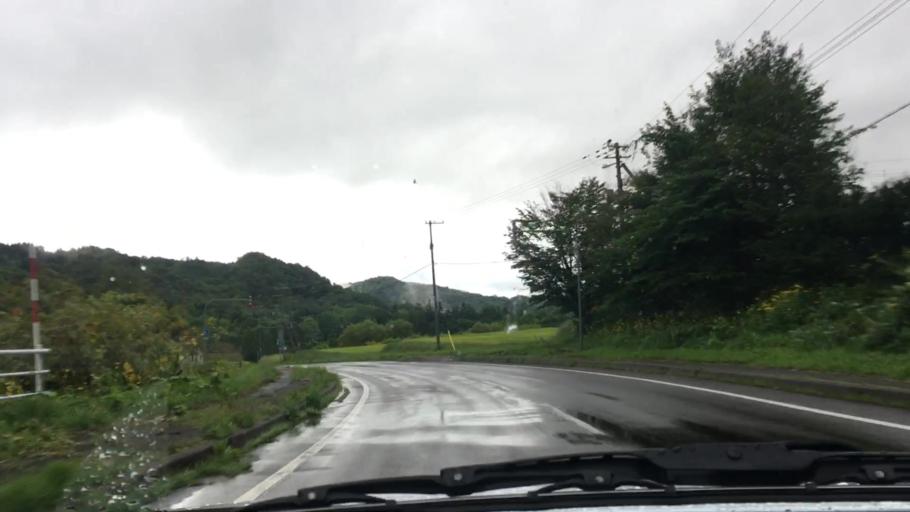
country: JP
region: Hokkaido
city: Niseko Town
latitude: 42.6524
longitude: 140.7389
